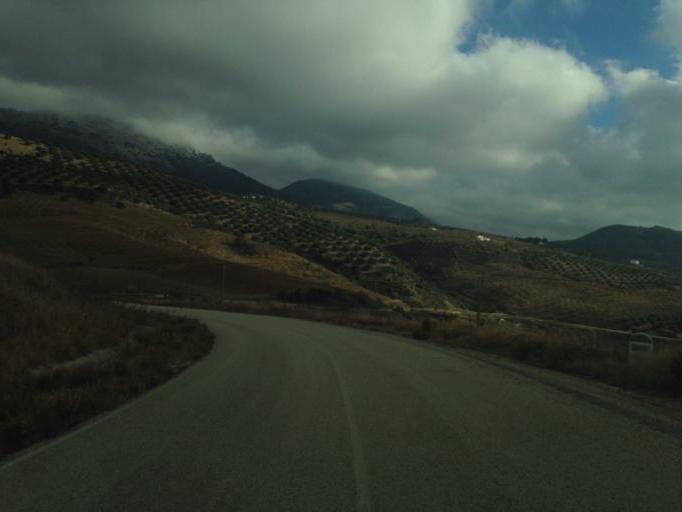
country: ES
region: Andalusia
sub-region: Provincia de Malaga
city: Colmenar
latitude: 36.9320
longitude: -4.3858
